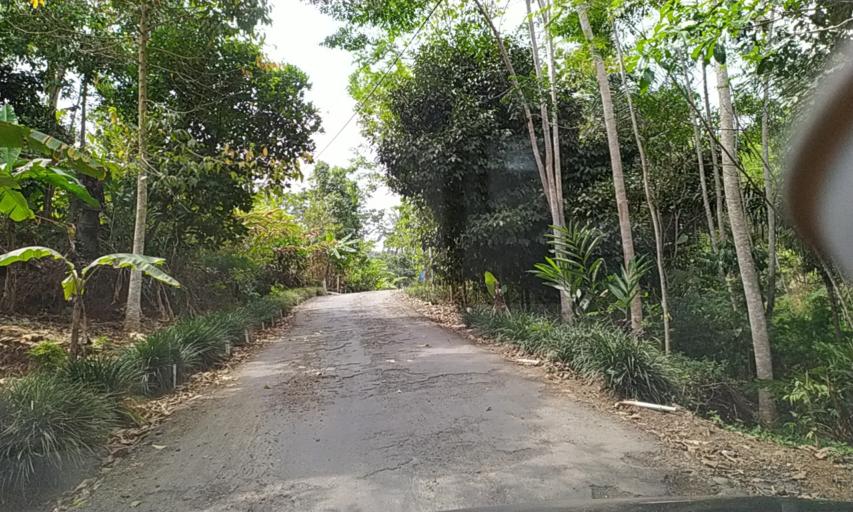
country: ID
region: Central Java
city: Kubang
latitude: -7.2731
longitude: 108.6442
